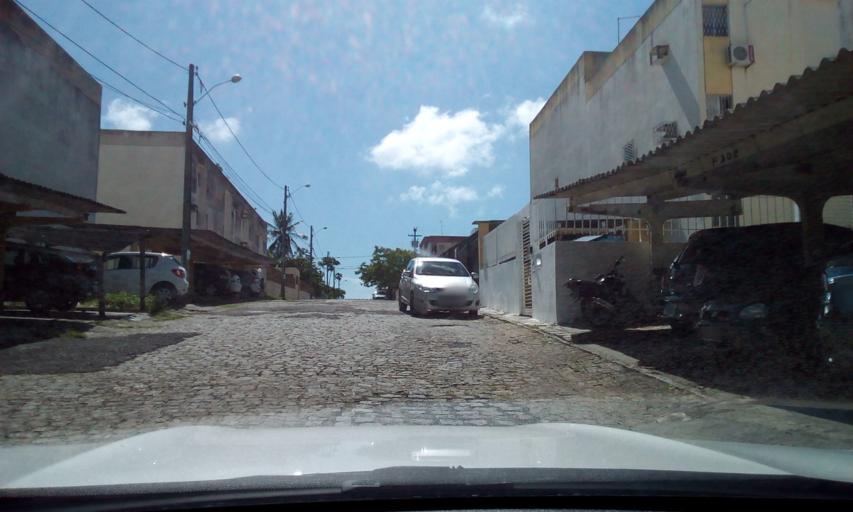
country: BR
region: Paraiba
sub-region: Joao Pessoa
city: Joao Pessoa
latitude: -7.1102
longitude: -34.8728
